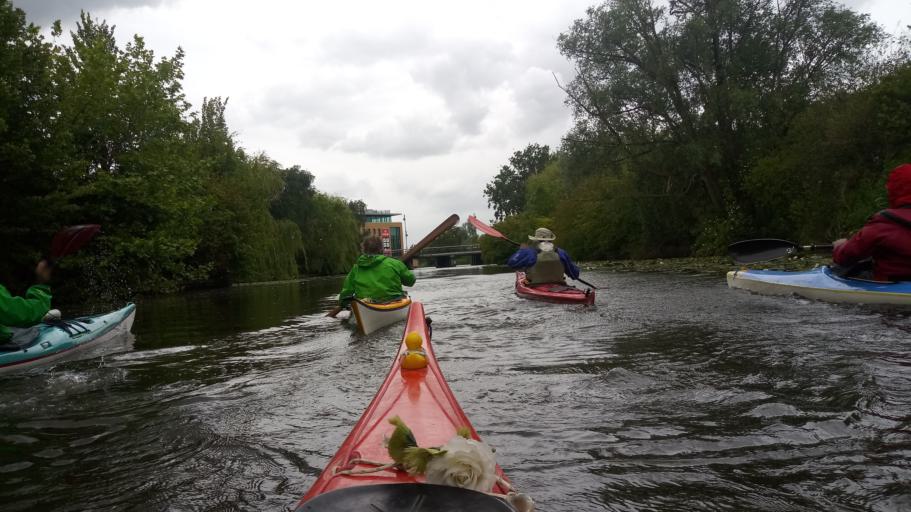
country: NL
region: North Holland
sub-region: Gemeente Enkhuizen
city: Enkhuizen
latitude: 52.6947
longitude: 5.2328
